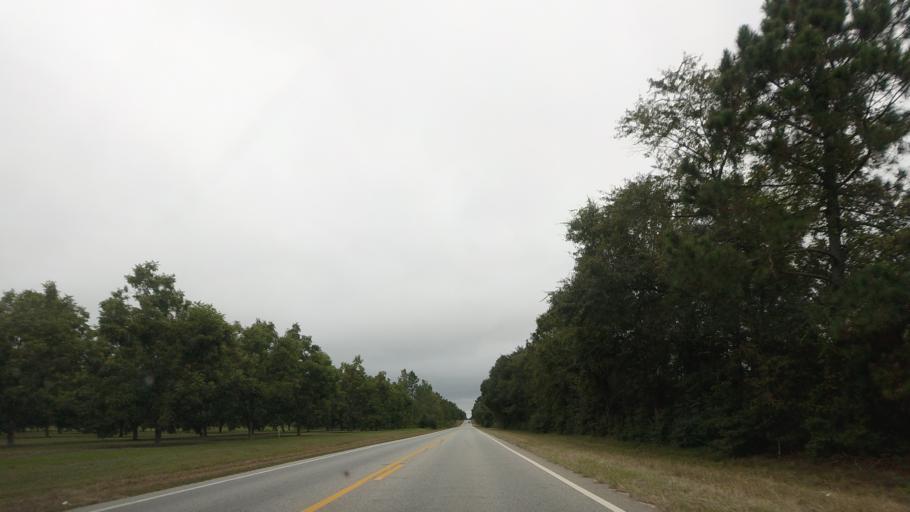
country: US
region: Georgia
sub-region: Berrien County
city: Ray City
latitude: 31.1040
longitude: -83.2087
